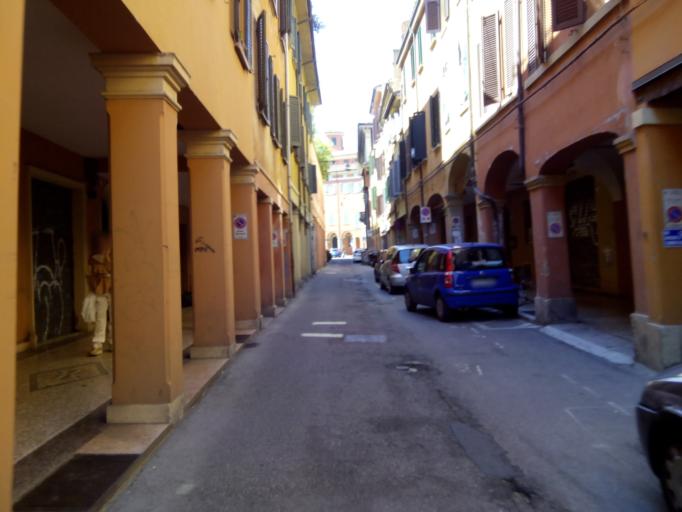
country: IT
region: Emilia-Romagna
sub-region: Provincia di Bologna
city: Bologna
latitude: 44.4880
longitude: 11.3543
